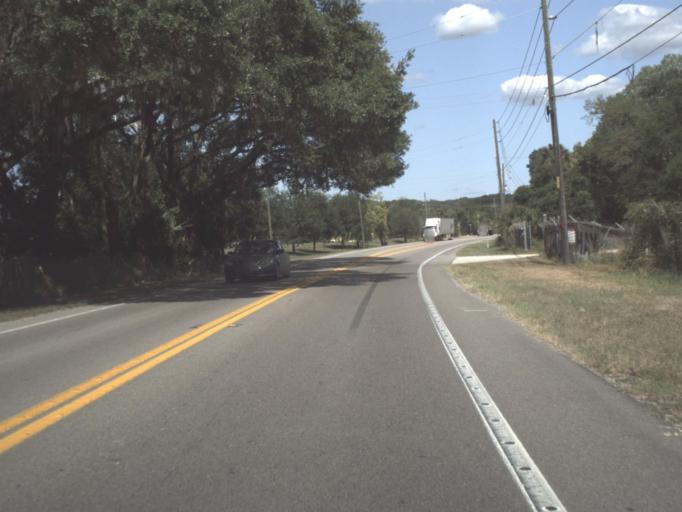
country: US
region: Florida
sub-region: Lake County
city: Mount Dora
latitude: 28.8000
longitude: -81.6165
